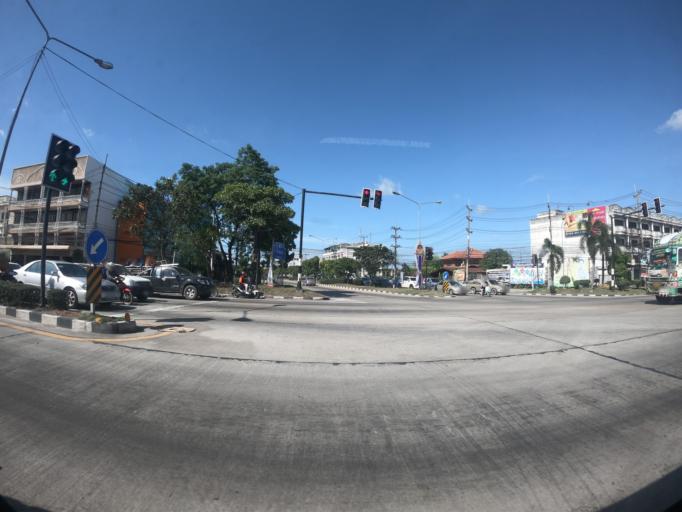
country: TH
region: Nakhon Nayok
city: Ban Na
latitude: 14.2598
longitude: 101.0733
